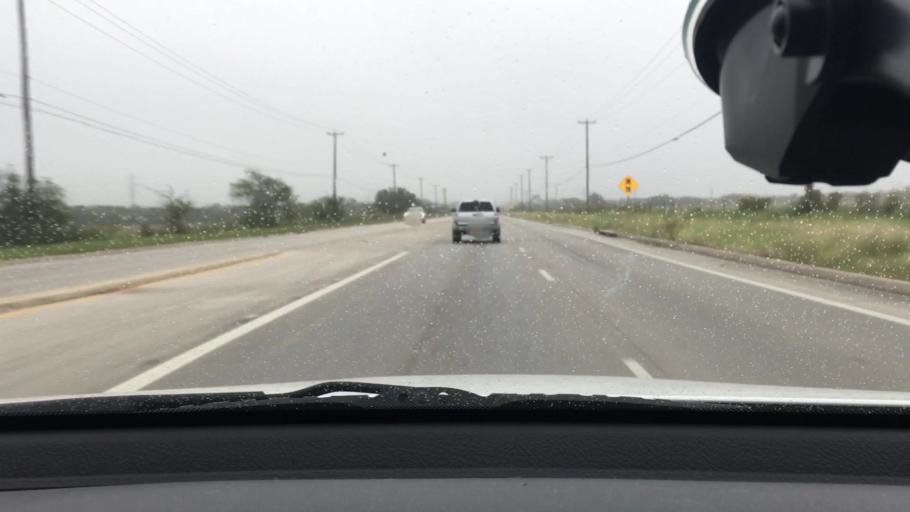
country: US
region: Texas
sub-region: Bexar County
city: Selma
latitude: 29.6019
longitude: -98.3325
